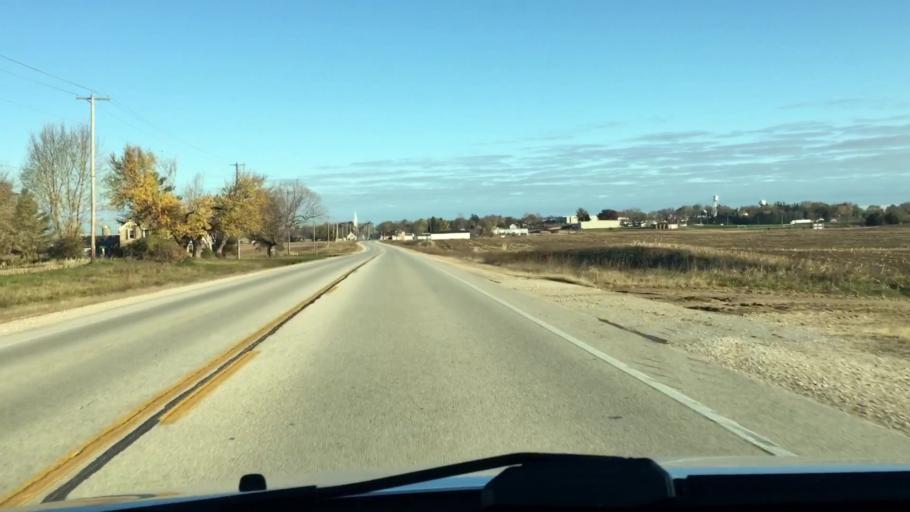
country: US
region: Wisconsin
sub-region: Dodge County
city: Lomira
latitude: 43.5783
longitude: -88.4499
